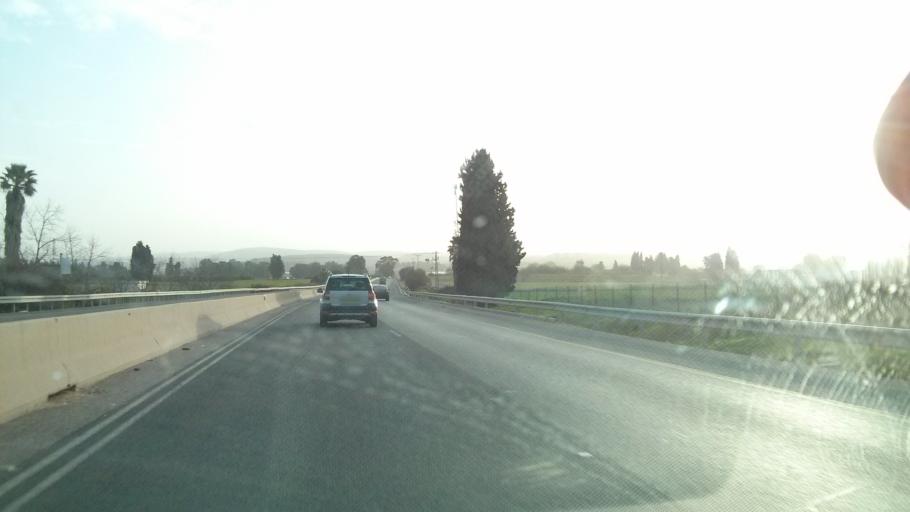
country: PS
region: West Bank
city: Nazlat `Isa
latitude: 32.4692
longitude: 35.0007
